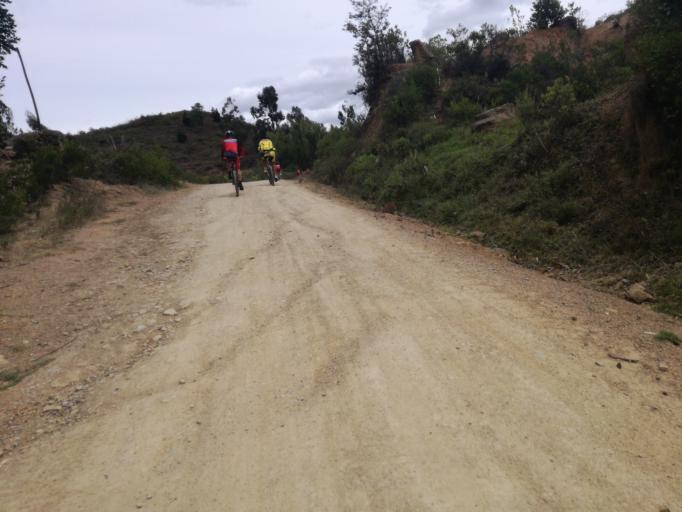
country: CO
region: Boyaca
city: Socha Viejo
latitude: 6.0123
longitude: -72.6837
